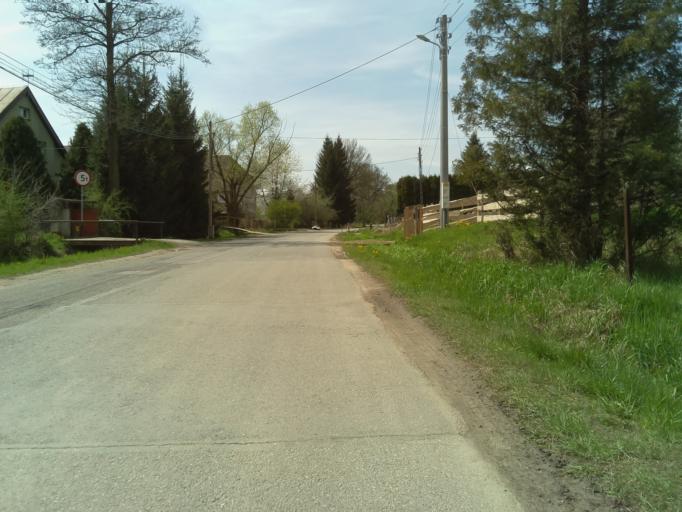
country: PL
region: Lower Silesian Voivodeship
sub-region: Powiat swidnicki
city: Swiebodzice
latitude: 50.8327
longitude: 16.3368
